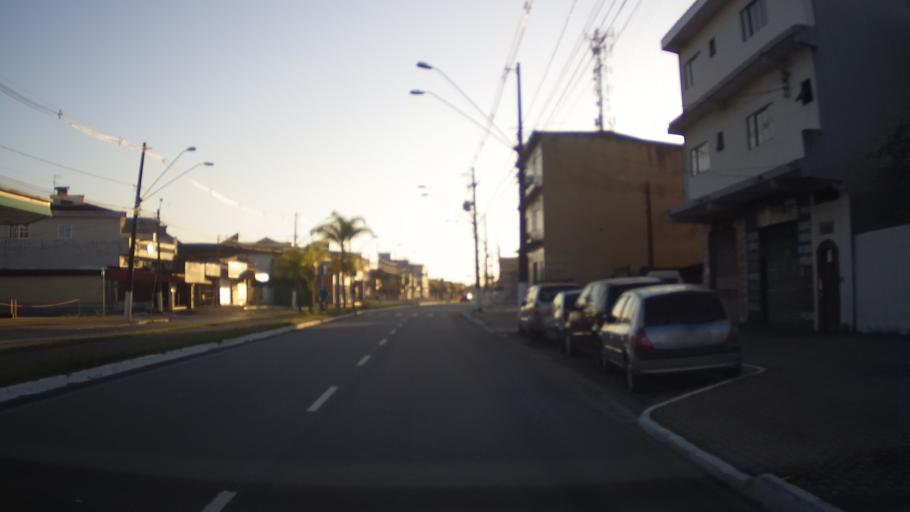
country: BR
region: Sao Paulo
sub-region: Praia Grande
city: Praia Grande
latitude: -24.0359
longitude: -46.5052
